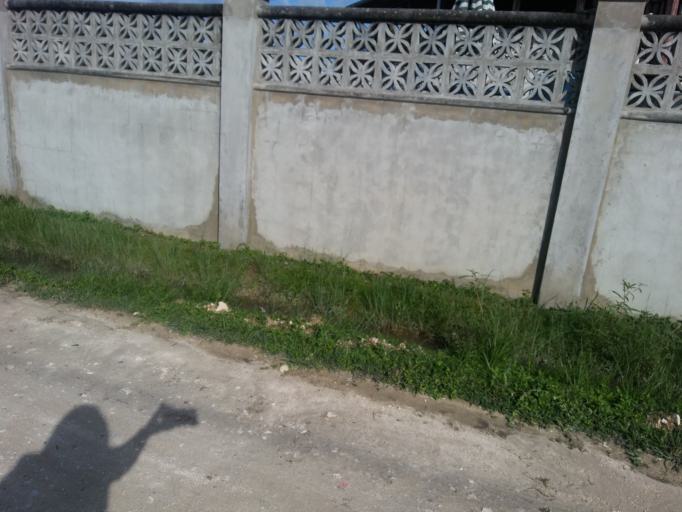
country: BZ
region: Belize
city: Belize City
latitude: 17.5708
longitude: -88.4187
